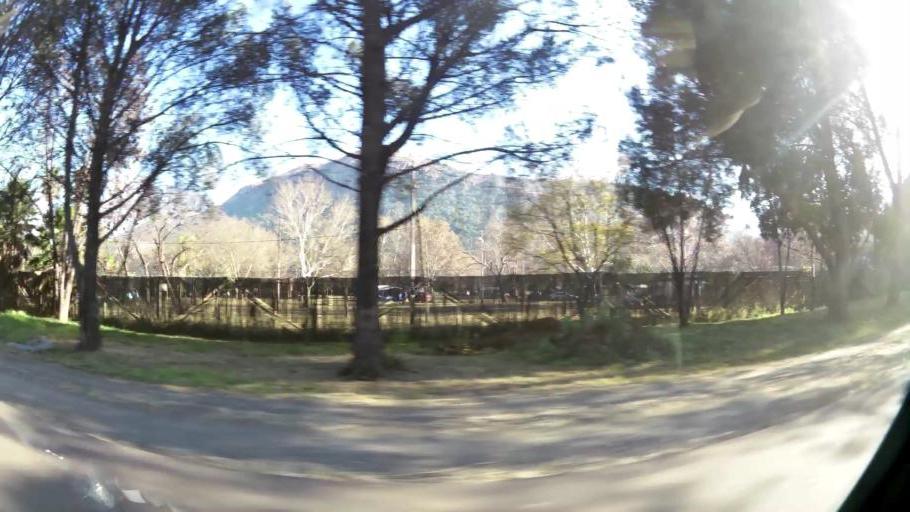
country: ZA
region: Gauteng
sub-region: City of Tshwane Metropolitan Municipality
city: Pretoria
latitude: -25.6969
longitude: 28.1852
